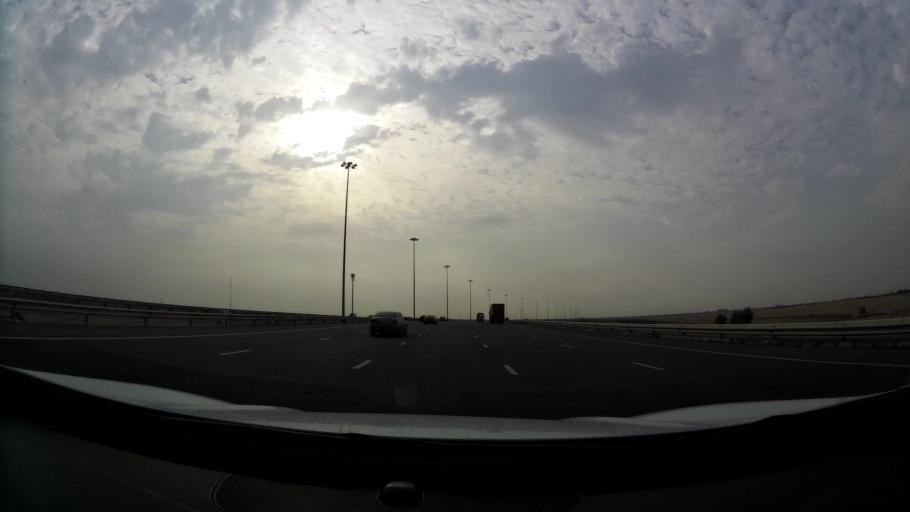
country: AE
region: Abu Dhabi
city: Abu Dhabi
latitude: 24.5432
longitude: 54.4805
